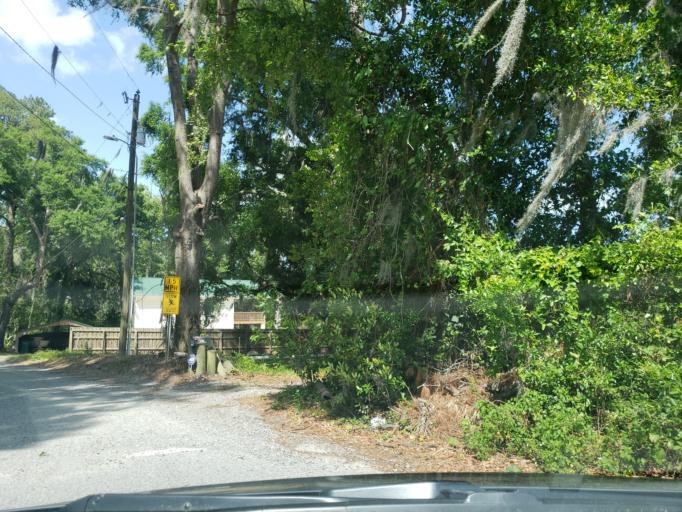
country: US
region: Georgia
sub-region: Chatham County
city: Thunderbolt
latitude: 32.0180
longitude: -81.0622
